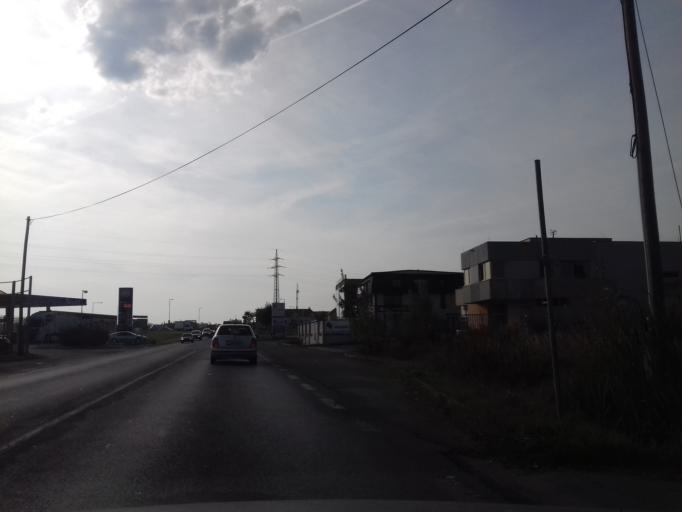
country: CZ
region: Central Bohemia
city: Vestec
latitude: 49.9933
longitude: 14.4887
